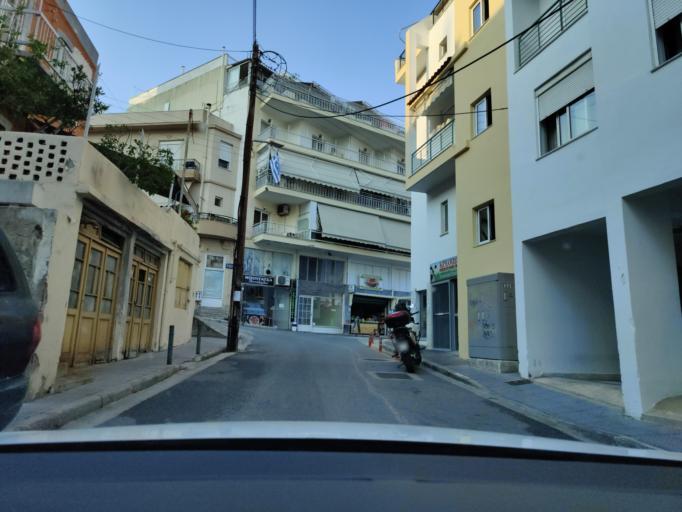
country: GR
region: East Macedonia and Thrace
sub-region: Nomos Kavalas
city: Kavala
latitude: 40.9387
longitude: 24.4032
